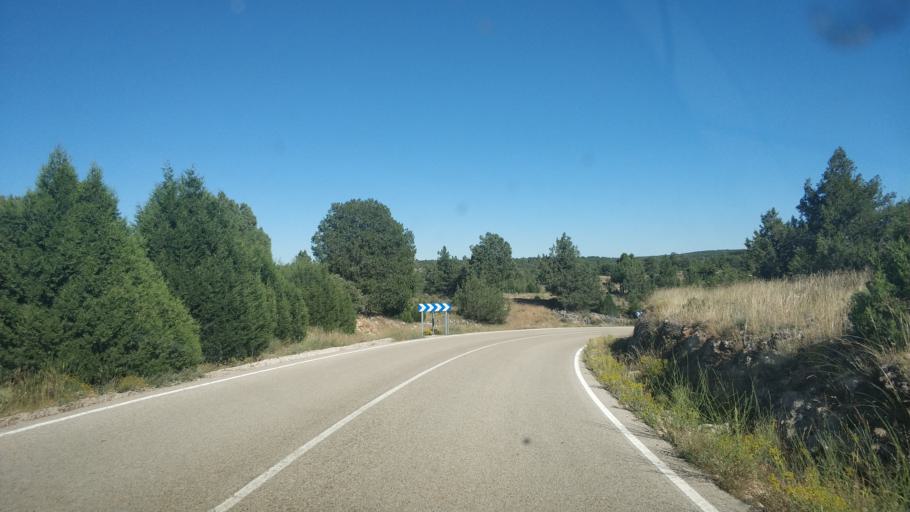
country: ES
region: Castille and Leon
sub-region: Provincia de Soria
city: Liceras
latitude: 41.4424
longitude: -3.2152
